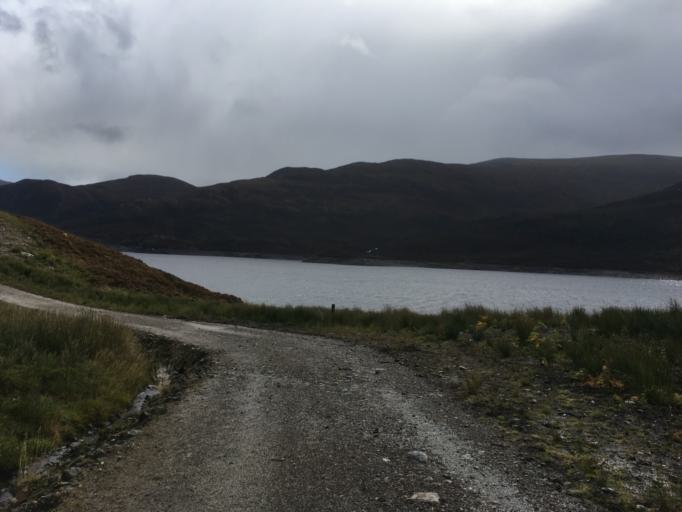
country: GB
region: Scotland
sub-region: Highland
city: Spean Bridge
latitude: 57.3412
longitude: -4.9781
